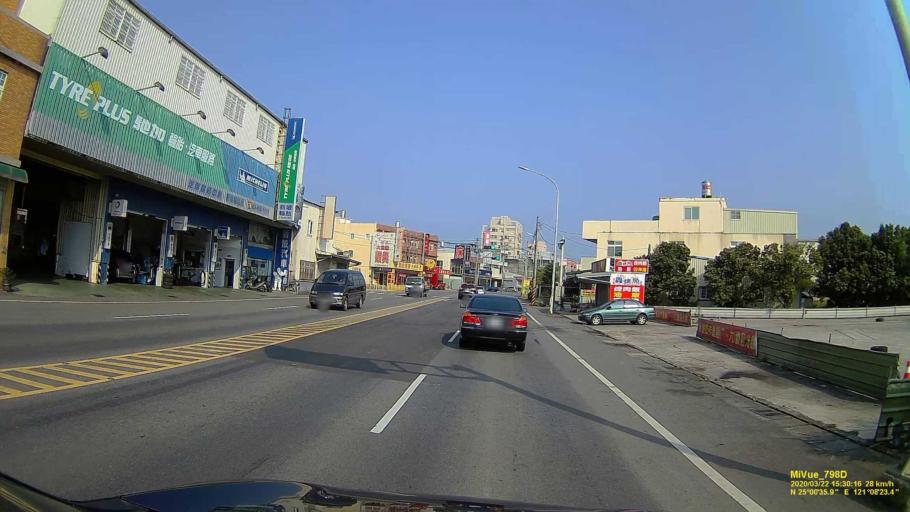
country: TW
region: Taiwan
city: Taoyuan City
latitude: 25.0099
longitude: 121.1399
